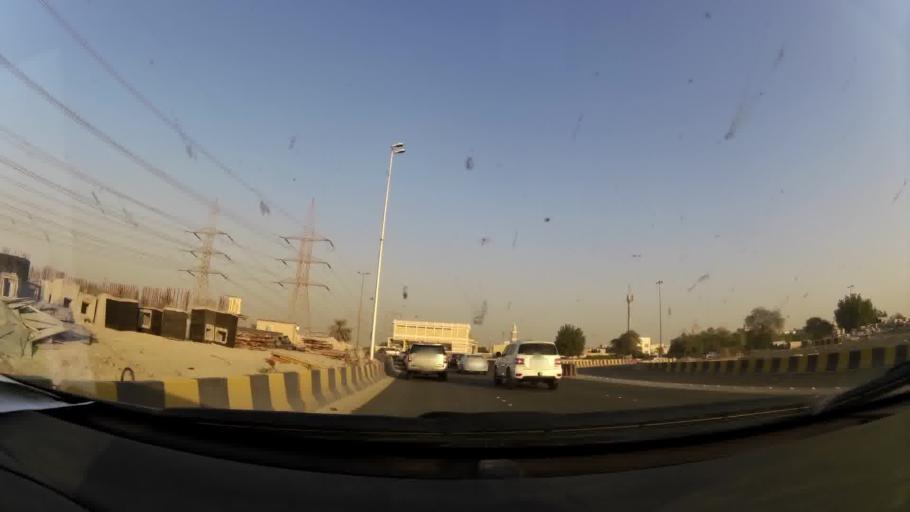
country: KW
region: Al Asimah
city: Ar Rabiyah
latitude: 29.2939
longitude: 47.8638
